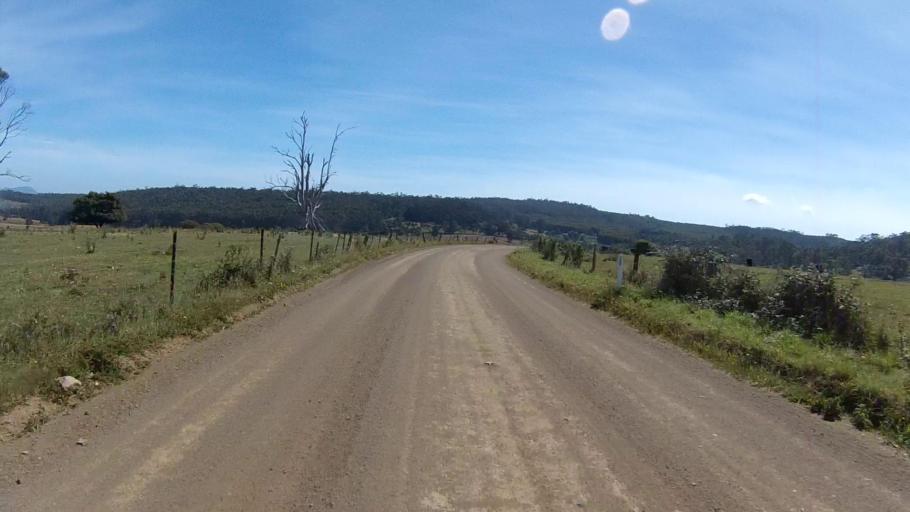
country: AU
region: Tasmania
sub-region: Sorell
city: Sorell
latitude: -42.7220
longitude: 147.7444
